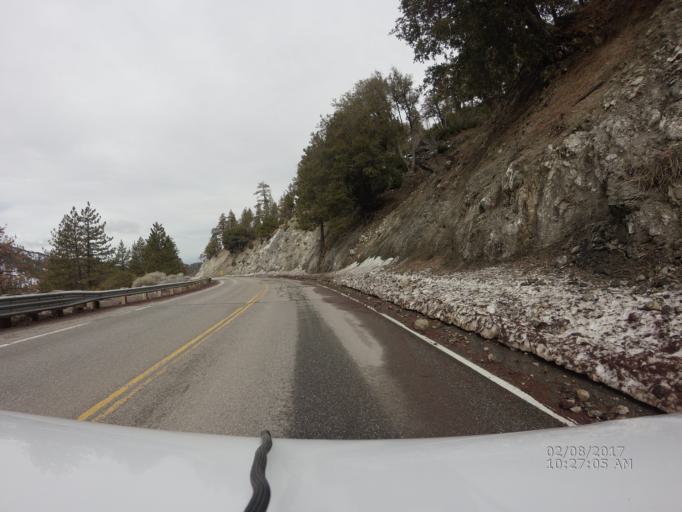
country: US
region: California
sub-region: San Bernardino County
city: Pinon Hills
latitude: 34.3866
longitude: -117.7060
